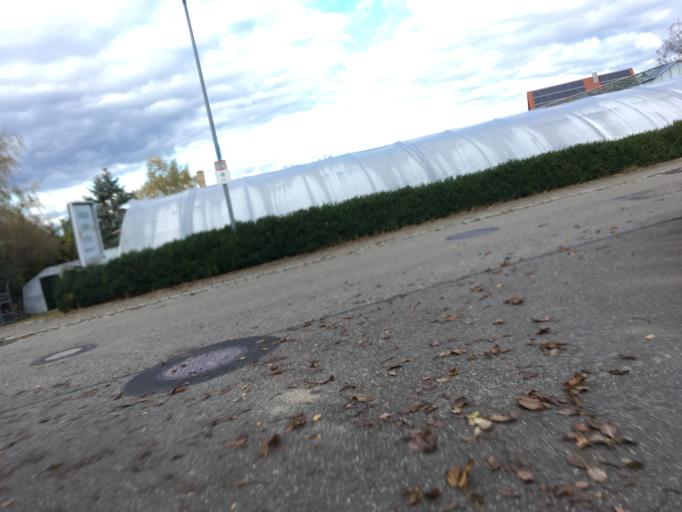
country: DE
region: Baden-Wuerttemberg
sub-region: Regierungsbezirk Stuttgart
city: Untermunkheim
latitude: 49.2016
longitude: 9.7382
